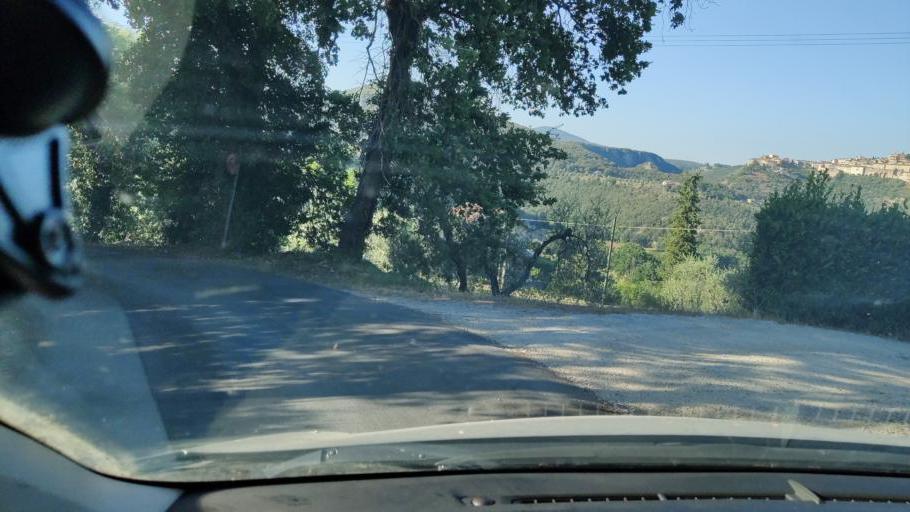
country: IT
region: Umbria
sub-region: Provincia di Terni
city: Amelia
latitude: 42.5438
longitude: 12.3996
